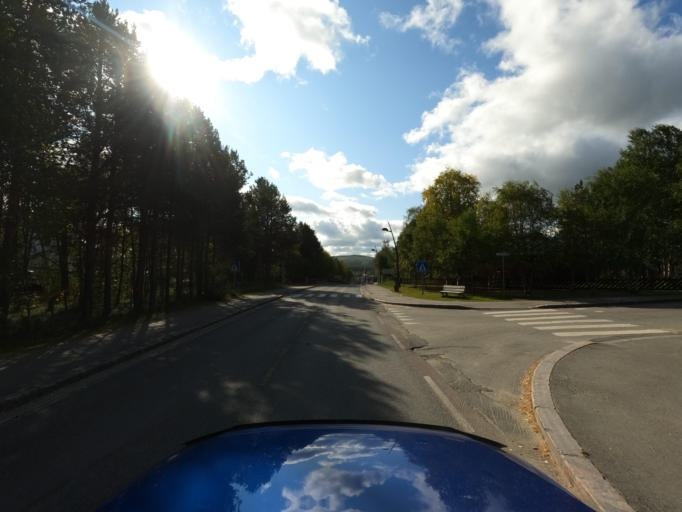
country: NO
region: Finnmark Fylke
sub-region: Karasjok
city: Karasjohka
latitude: 69.4704
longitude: 25.5102
